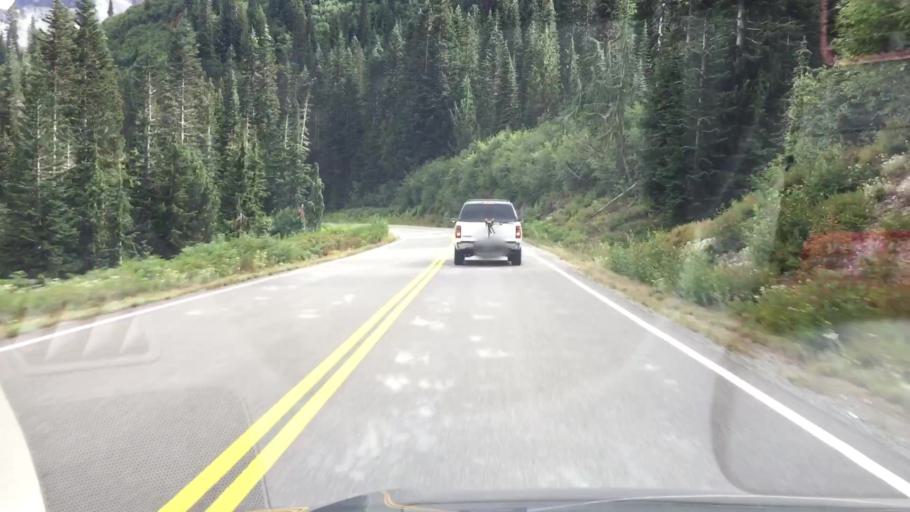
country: US
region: Washington
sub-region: Pierce County
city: Buckley
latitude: 46.7697
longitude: -121.7122
